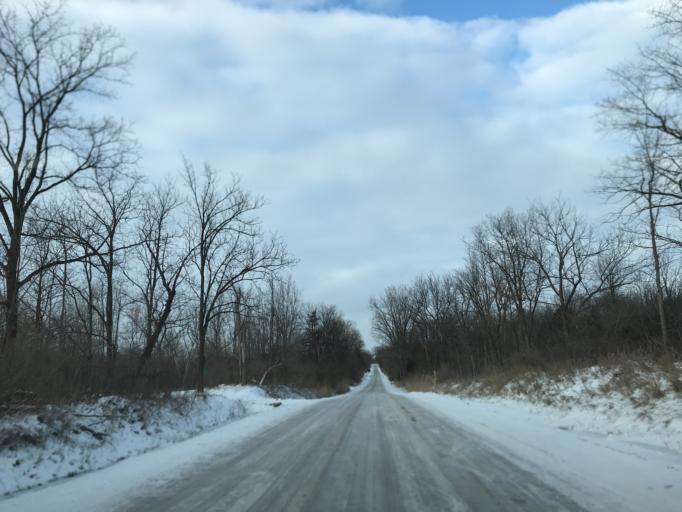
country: US
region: Michigan
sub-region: Oakland County
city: South Lyon
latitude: 42.4516
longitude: -83.5921
